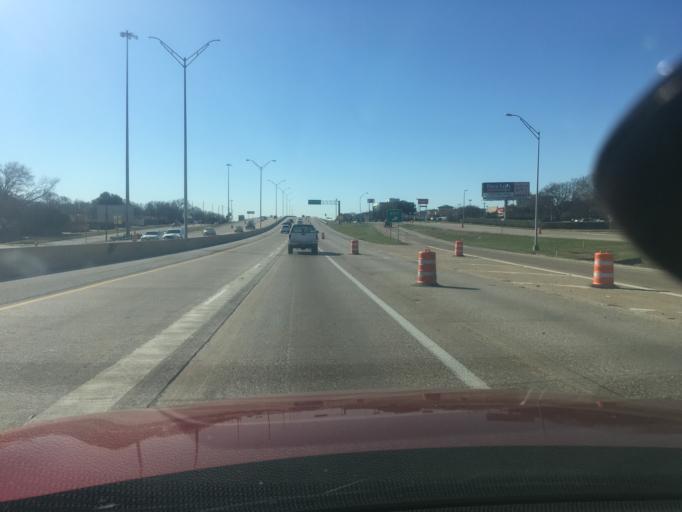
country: US
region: Texas
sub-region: Dallas County
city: Duncanville
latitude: 32.6805
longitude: -96.8536
